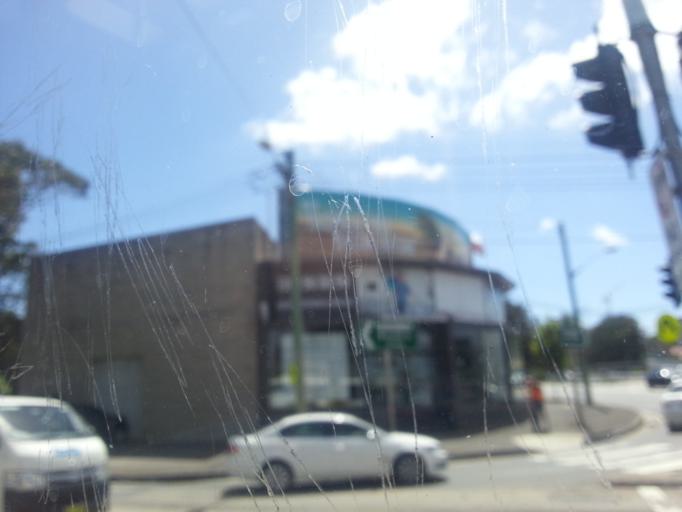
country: AU
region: New South Wales
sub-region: City of Sydney
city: Alexandria
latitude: -33.9055
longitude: 151.2027
